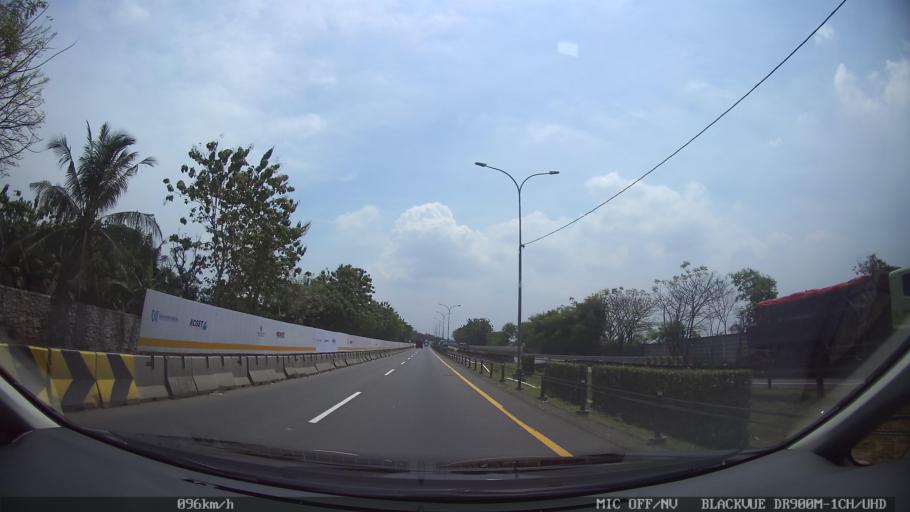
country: ID
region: Banten
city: Serang
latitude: -6.1384
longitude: 106.2269
